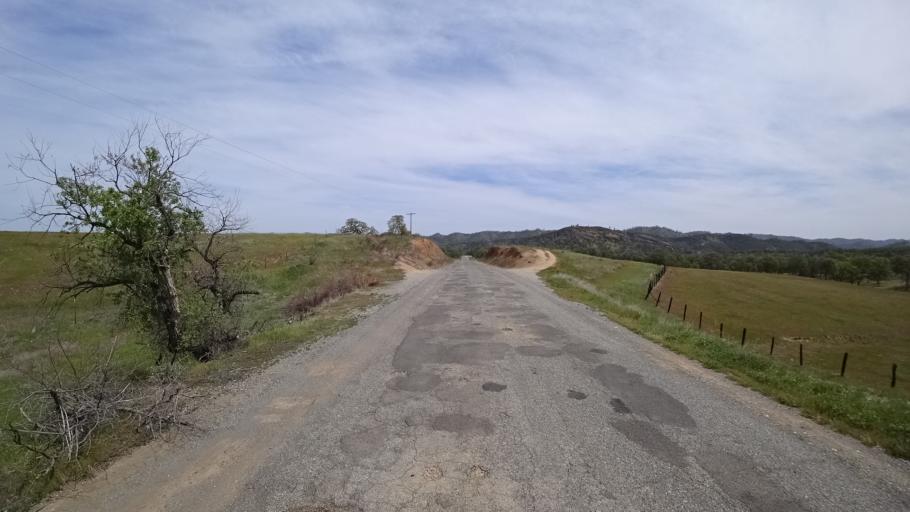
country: US
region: California
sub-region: Glenn County
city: Willows
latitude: 39.6062
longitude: -122.5524
